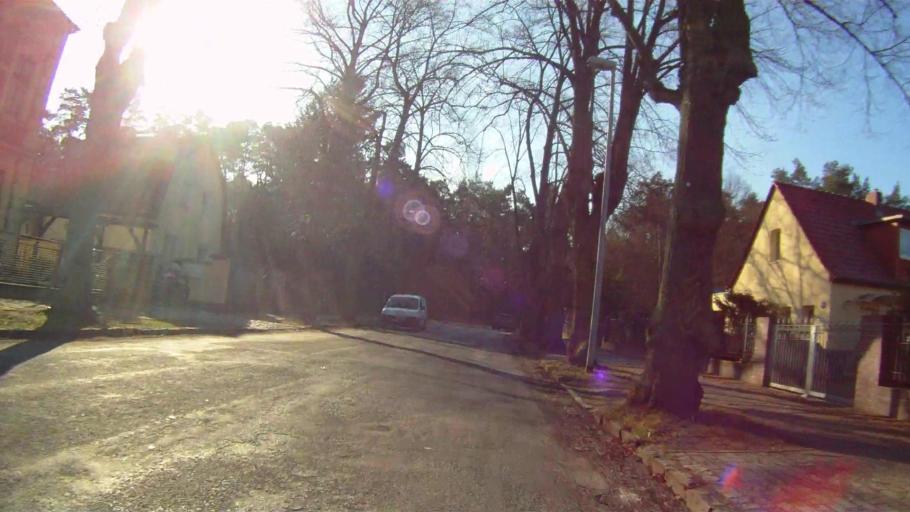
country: DE
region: Brandenburg
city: Schoneiche
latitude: 52.4553
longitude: 13.7017
